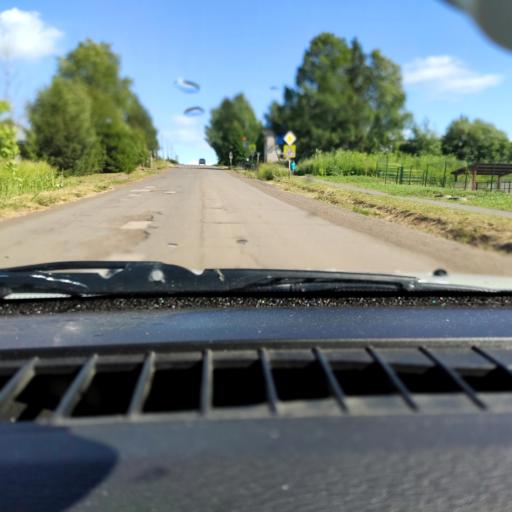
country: RU
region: Perm
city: Uinskoye
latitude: 57.1147
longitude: 56.5285
